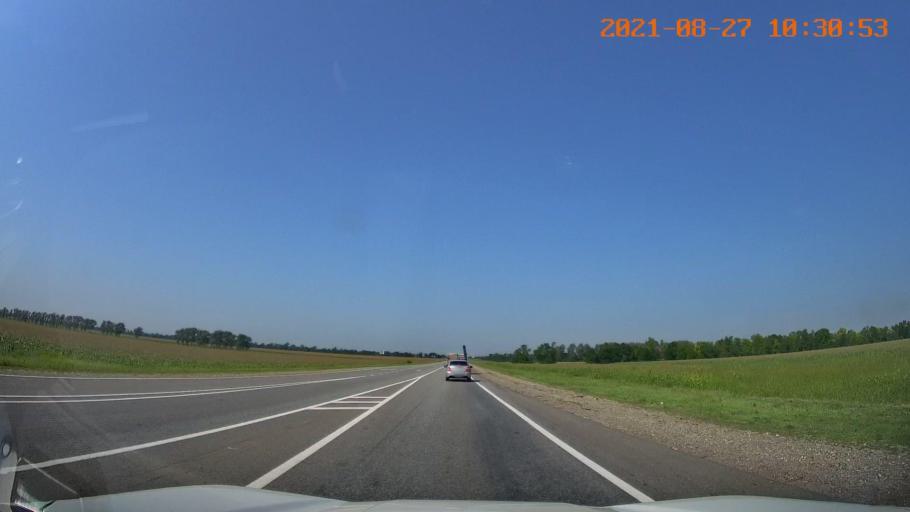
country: RU
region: Karachayevo-Cherkesiya
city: Kavkazskiy
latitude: 44.2628
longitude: 42.1715
